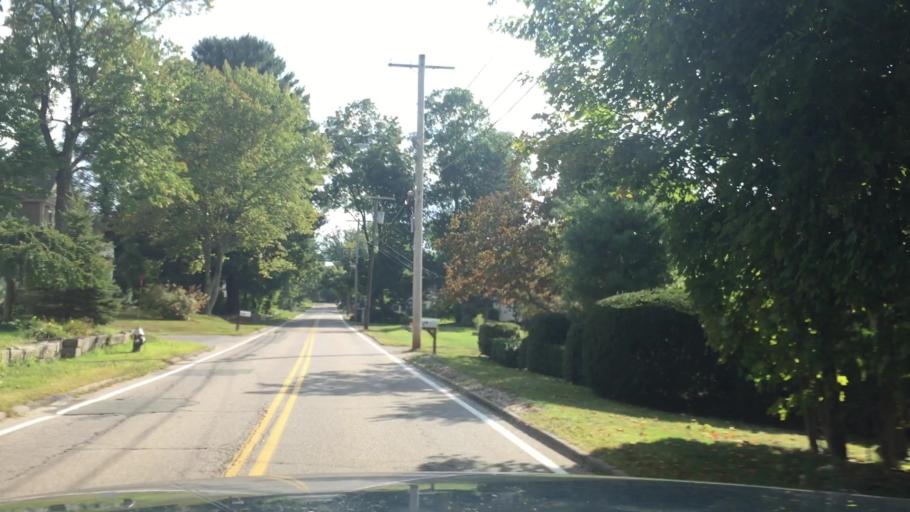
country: US
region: Massachusetts
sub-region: Norfolk County
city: Medway
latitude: 42.1551
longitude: -71.4235
